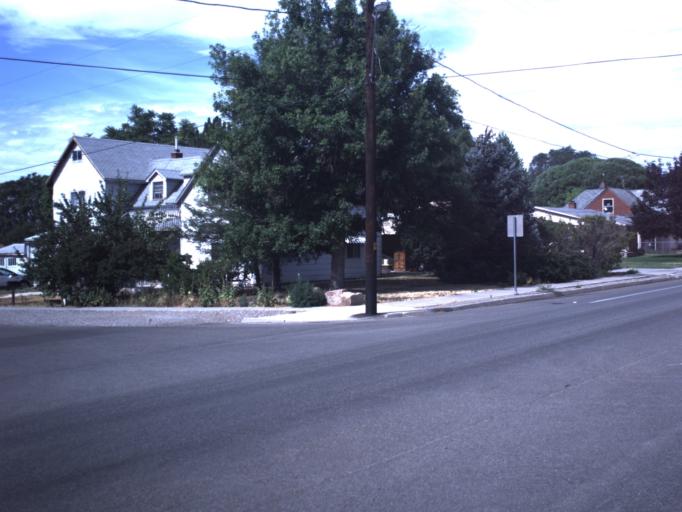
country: US
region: Utah
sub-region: Sevier County
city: Richfield
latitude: 38.7723
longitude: -112.0810
